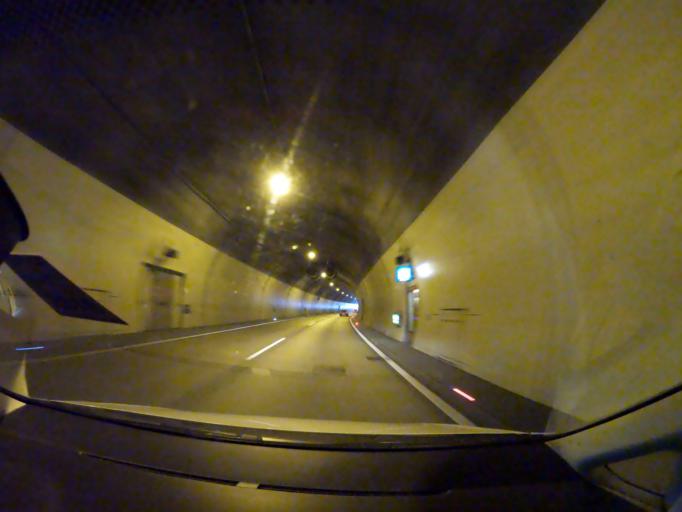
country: AT
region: Styria
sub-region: Politischer Bezirk Voitsberg
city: Modriach
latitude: 46.9775
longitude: 15.0887
